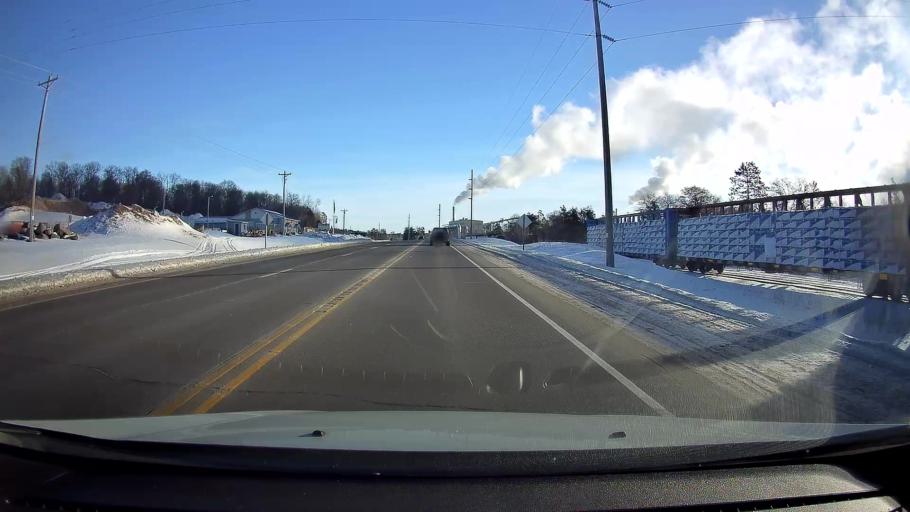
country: US
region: Wisconsin
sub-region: Sawyer County
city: Hayward
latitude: 45.9859
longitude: -91.5299
